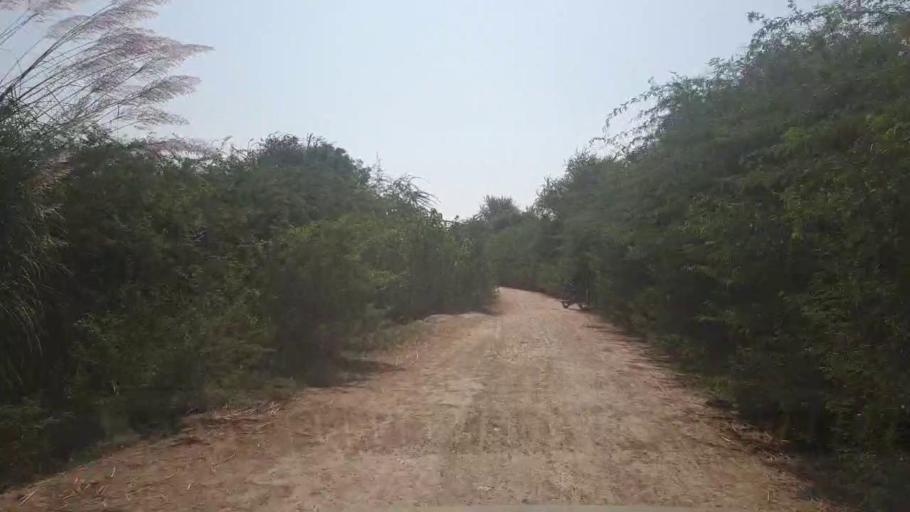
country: PK
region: Sindh
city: Badin
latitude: 24.6813
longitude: 68.8791
